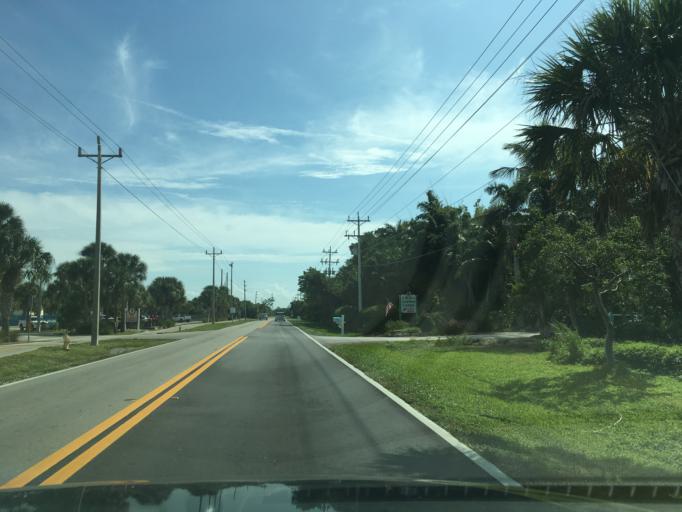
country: US
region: Florida
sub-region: Lee County
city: Saint James City
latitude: 26.4465
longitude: -82.1167
